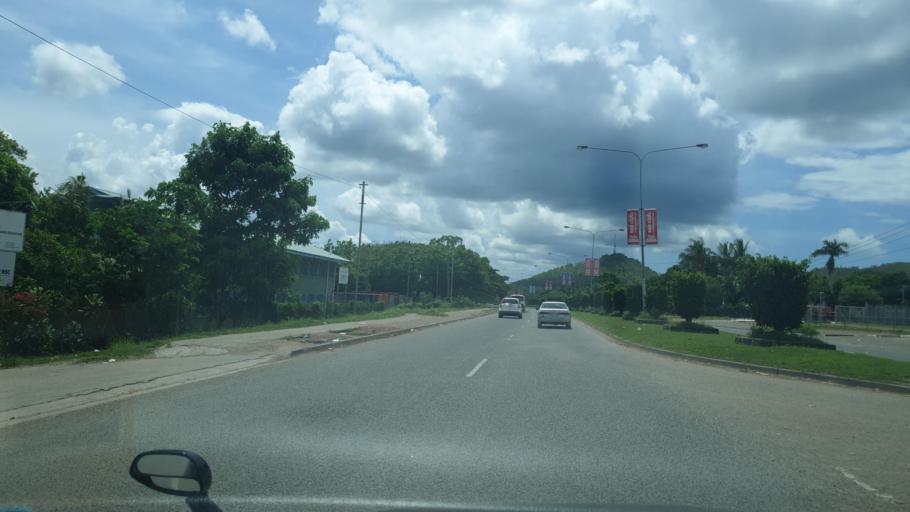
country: PG
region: National Capital
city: Port Moresby
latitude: -9.4004
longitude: 147.1612
